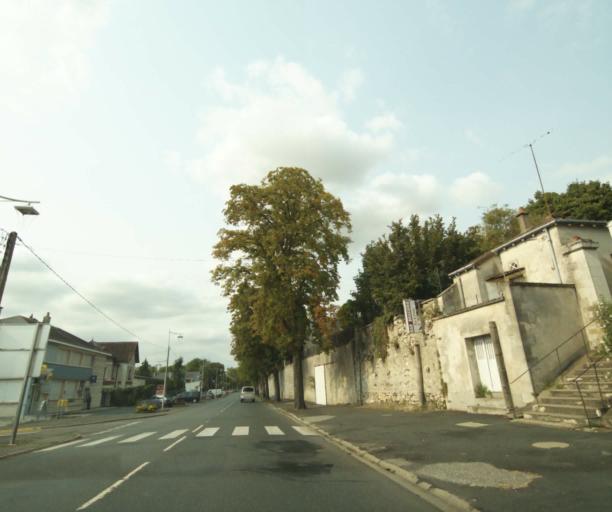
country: FR
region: Centre
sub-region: Departement de l'Indre
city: Chatillon-sur-Indre
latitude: 46.9858
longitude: 1.1730
